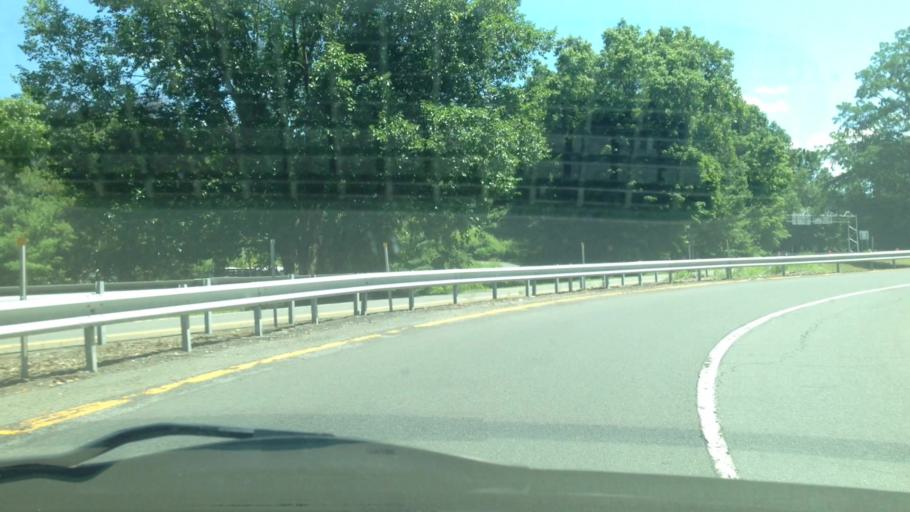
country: US
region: New York
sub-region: Ulster County
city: Lake Katrine
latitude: 41.9753
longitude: -73.9880
